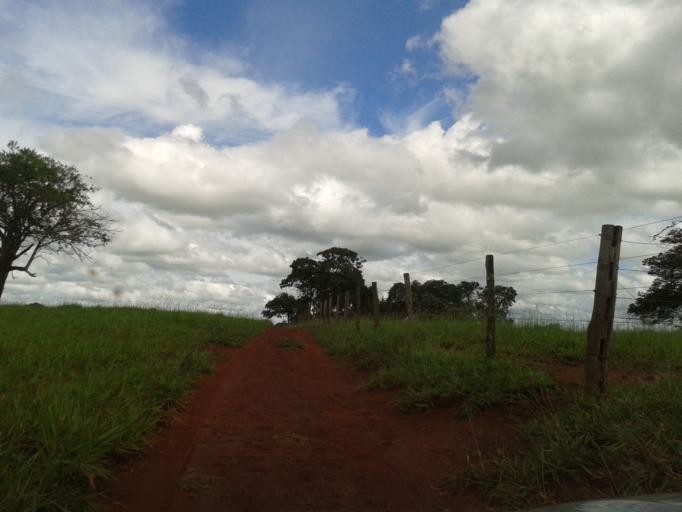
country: BR
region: Minas Gerais
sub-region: Capinopolis
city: Capinopolis
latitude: -18.7781
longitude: -49.7723
